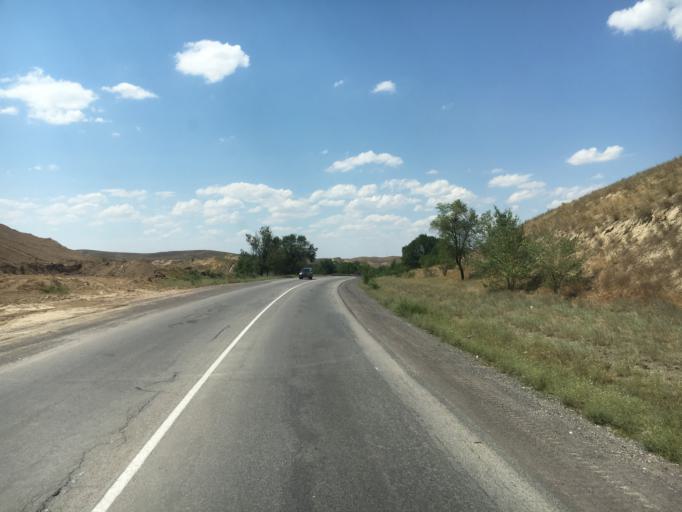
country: KZ
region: Almaty Oblysy
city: Burunday
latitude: 43.2918
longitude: 76.2374
